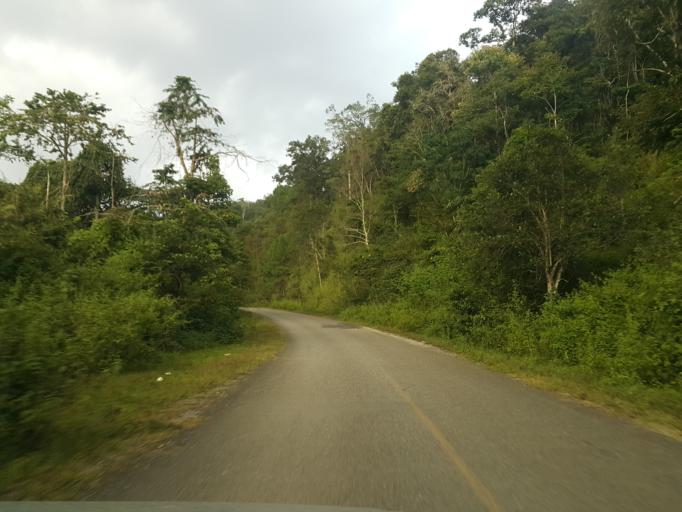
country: TH
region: Mae Hong Son
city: Khun Yuam
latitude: 18.7628
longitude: 98.1859
